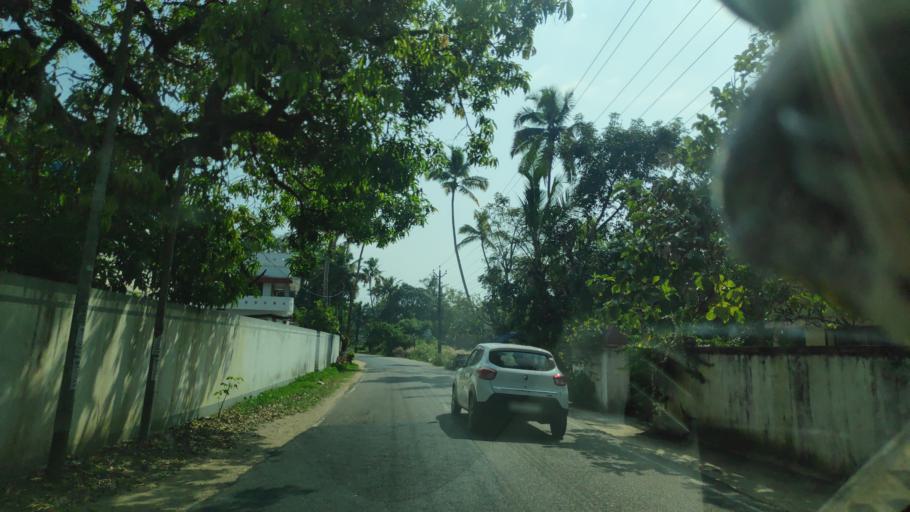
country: IN
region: Kerala
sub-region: Alappuzha
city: Shertallai
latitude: 9.6214
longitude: 76.3004
